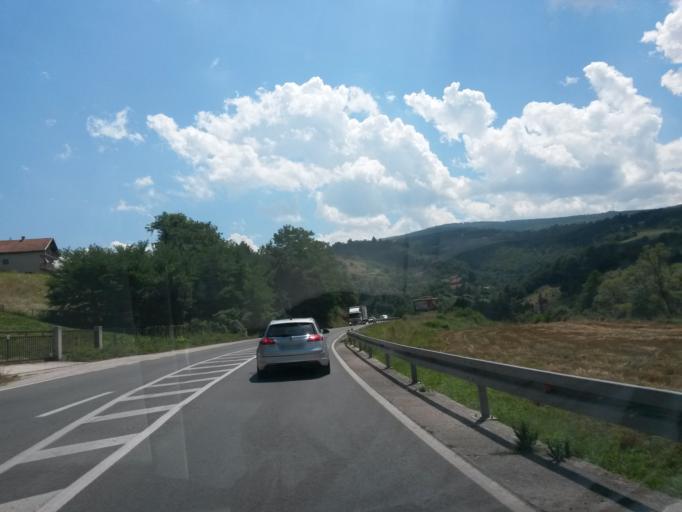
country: BA
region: Federation of Bosnia and Herzegovina
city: Turbe
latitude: 44.2358
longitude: 17.6107
